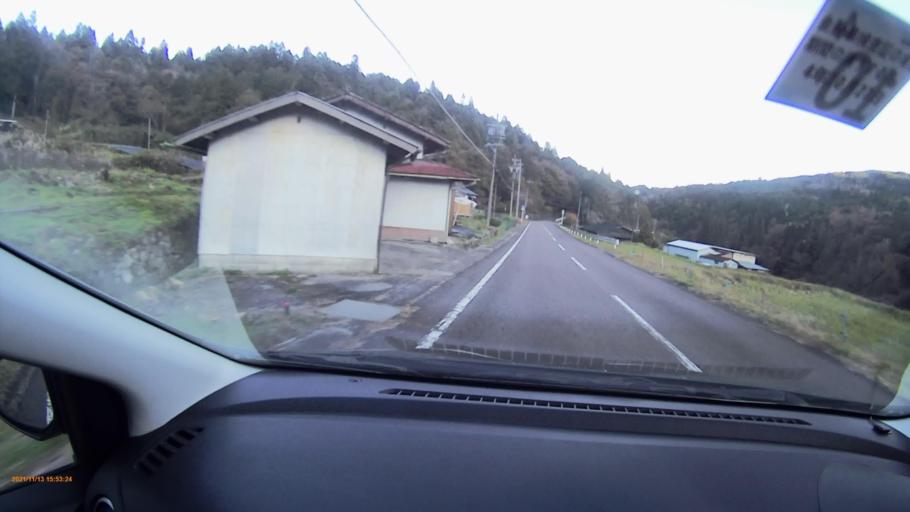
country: JP
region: Gifu
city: Nakatsugawa
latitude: 35.5972
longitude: 137.4376
